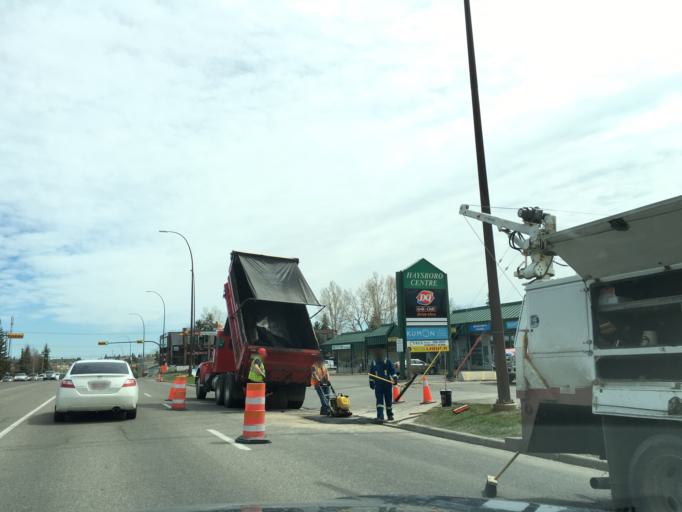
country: CA
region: Alberta
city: Calgary
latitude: 50.9796
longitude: -114.0846
